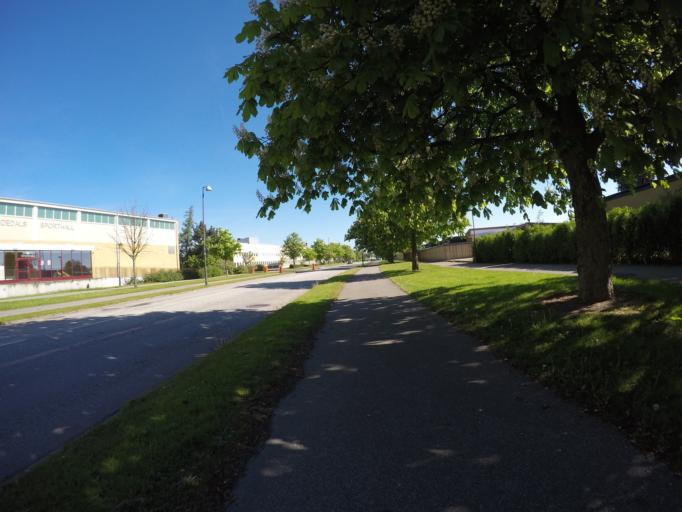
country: SE
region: Skane
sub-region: Burlovs Kommun
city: Arloev
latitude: 55.5893
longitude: 13.0705
